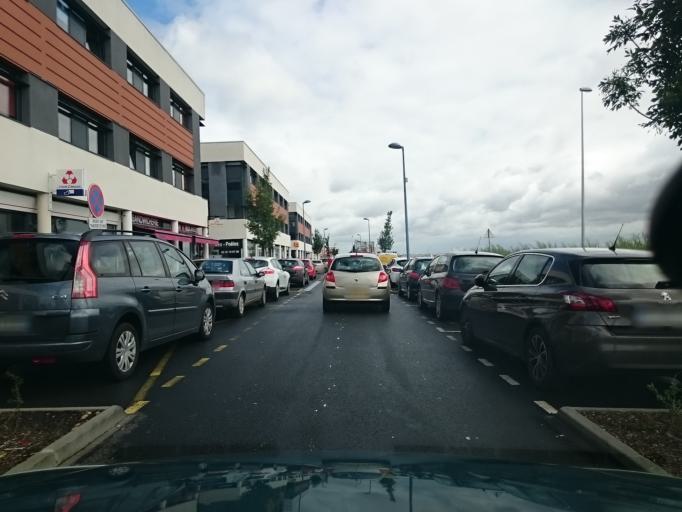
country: FR
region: Lower Normandy
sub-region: Departement du Calvados
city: Fleury-sur-Orne
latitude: 49.1398
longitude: -0.3764
